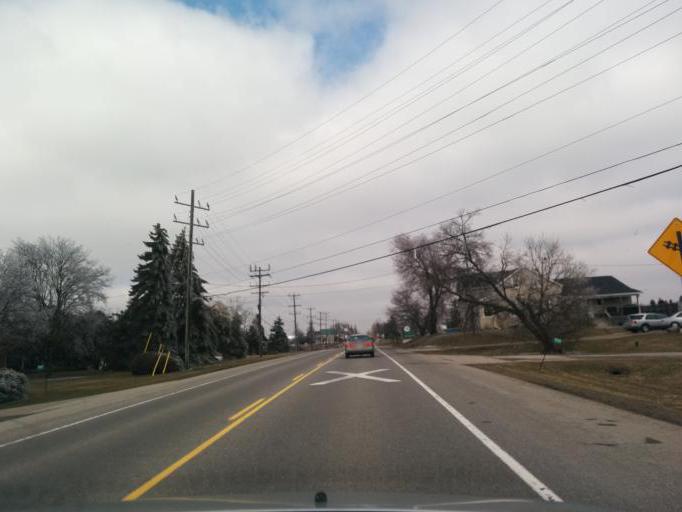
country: CA
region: Ontario
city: Waterloo
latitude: 43.5248
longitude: -80.5560
